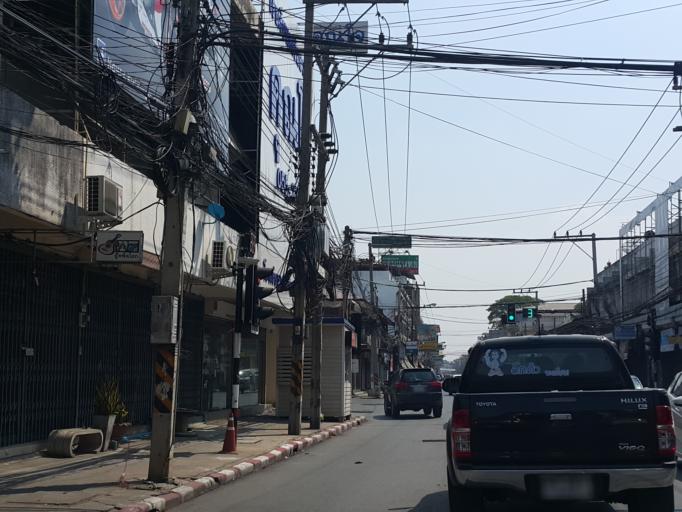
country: TH
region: Phitsanulok
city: Phitsanulok
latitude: 16.8114
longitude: 100.2607
